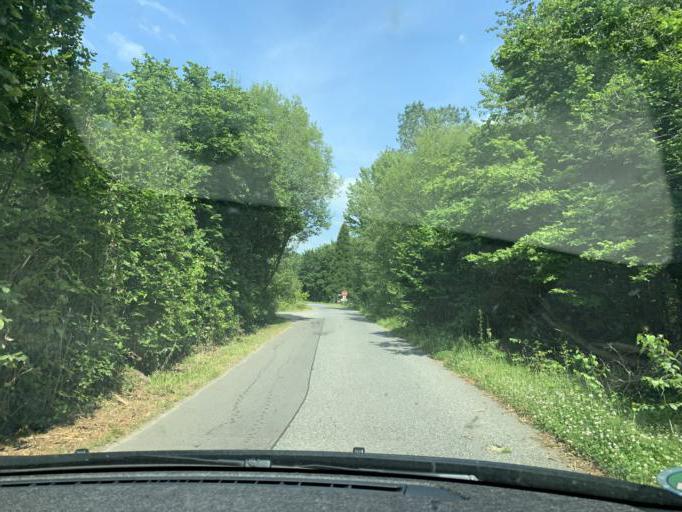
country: DE
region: North Rhine-Westphalia
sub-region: Regierungsbezirk Dusseldorf
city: Grevenbroich
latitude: 51.0525
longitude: 6.5581
